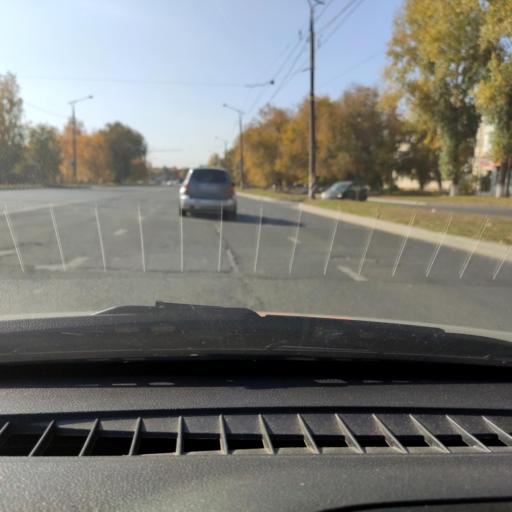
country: RU
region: Samara
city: Zhigulevsk
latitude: 53.4744
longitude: 49.4810
